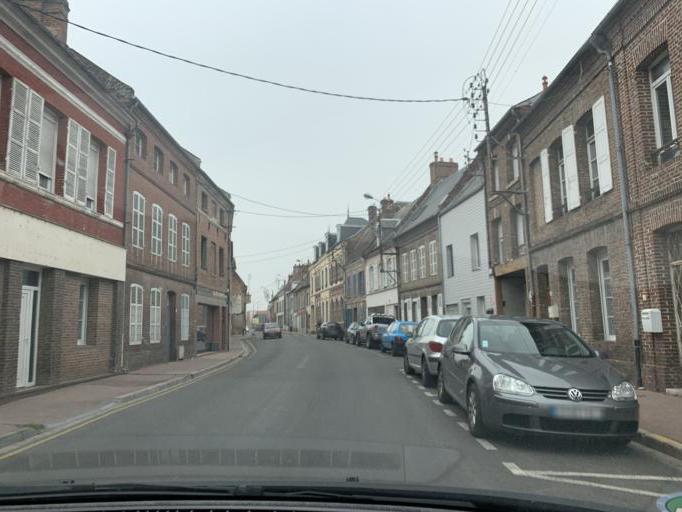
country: FR
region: Picardie
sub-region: Departement de la Somme
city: Abbeville
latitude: 50.1124
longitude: 1.8280
